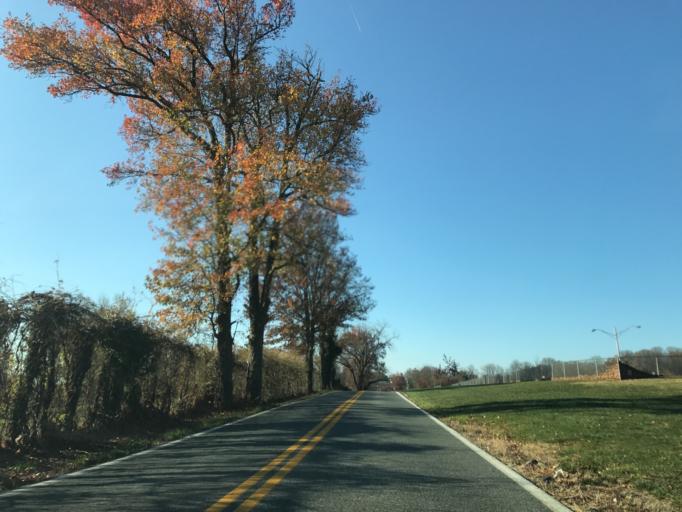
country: US
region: Maryland
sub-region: Baltimore County
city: Catonsville
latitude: 39.2583
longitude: -76.7275
